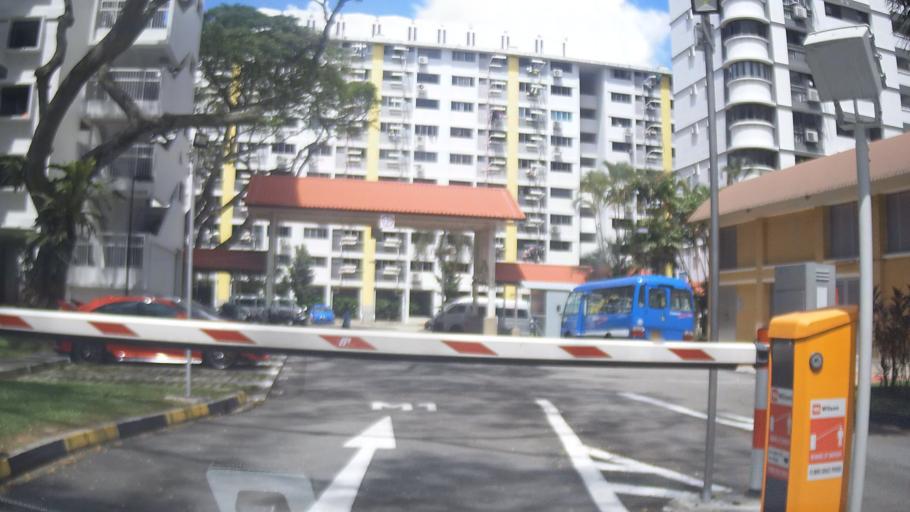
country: SG
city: Singapore
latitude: 1.3234
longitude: 103.8881
